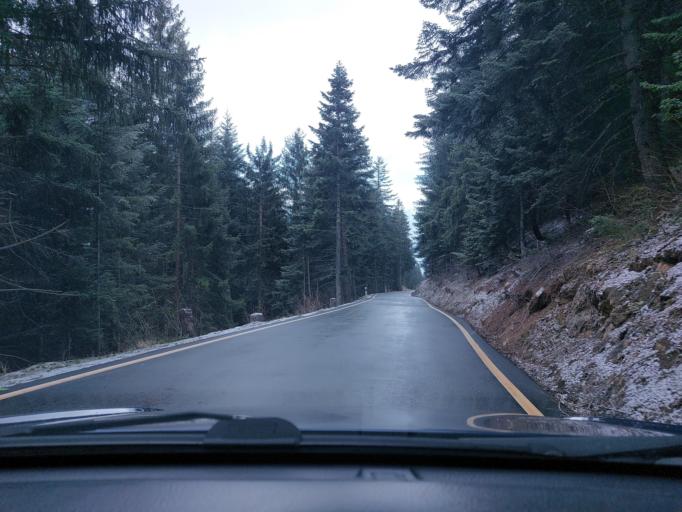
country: CH
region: Valais
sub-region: Sion District
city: Saviese
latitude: 46.2823
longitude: 7.3261
